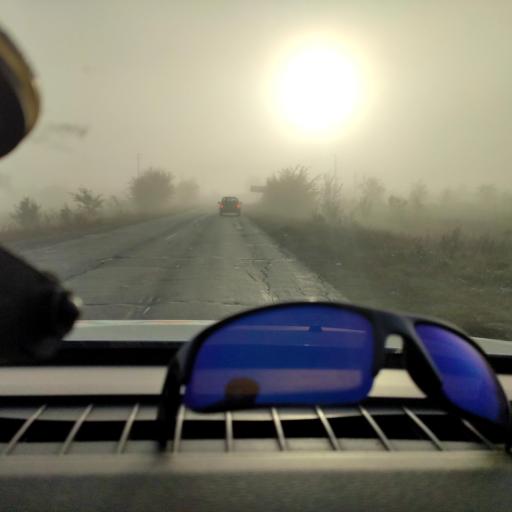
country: RU
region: Samara
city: Chapayevsk
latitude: 53.0001
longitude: 49.7650
